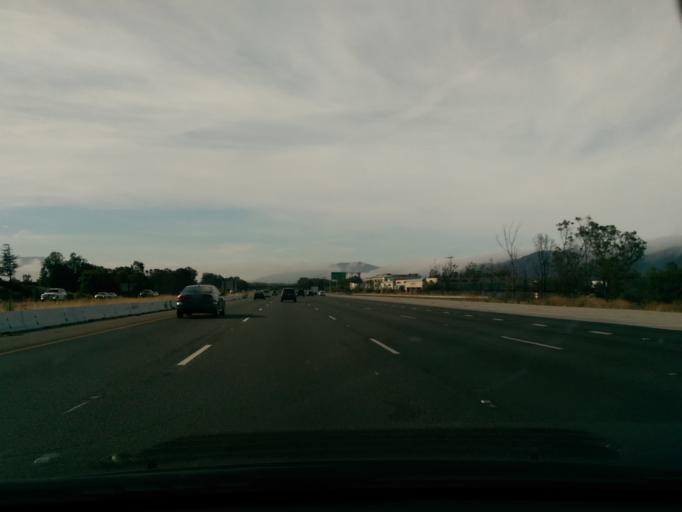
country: US
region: California
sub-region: Riverside County
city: Murrieta Hot Springs
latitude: 33.5298
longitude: -117.1681
